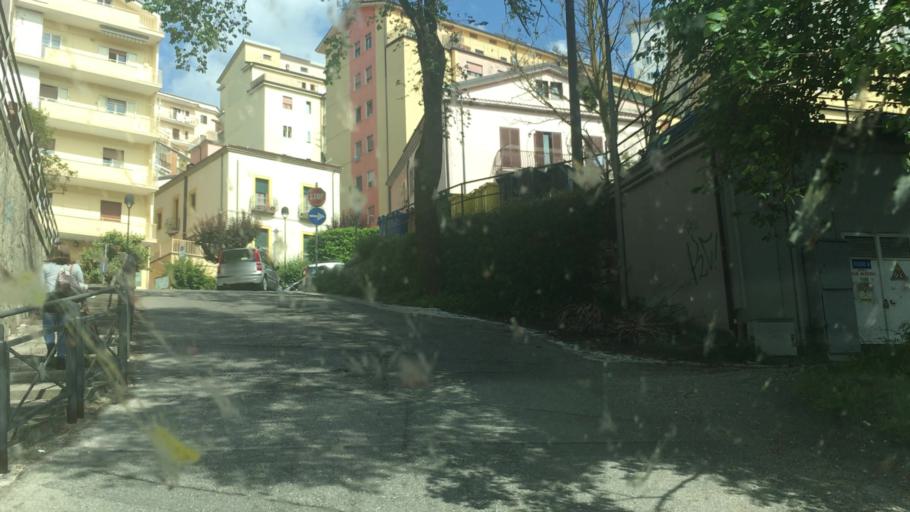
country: IT
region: Basilicate
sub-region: Provincia di Potenza
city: Potenza
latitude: 40.6417
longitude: 15.8042
